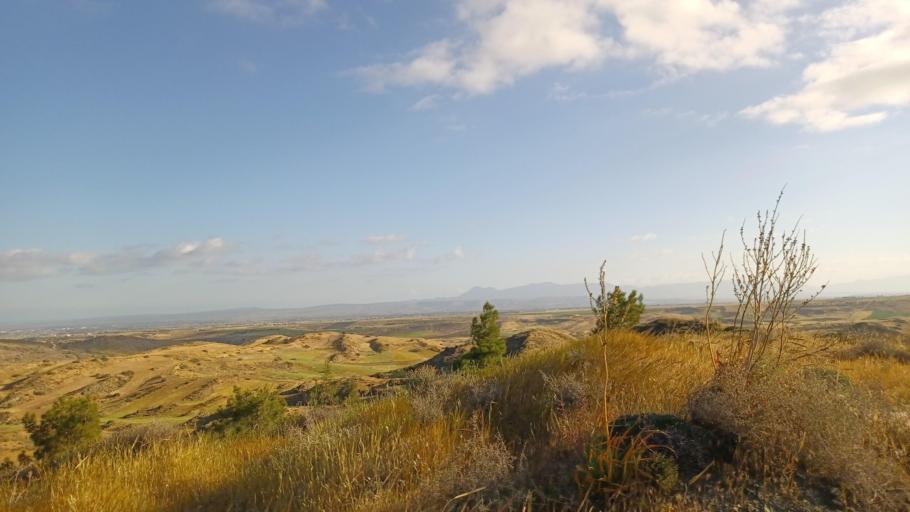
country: CY
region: Lefkosia
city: Peristerona
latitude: 35.0732
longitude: 33.0429
